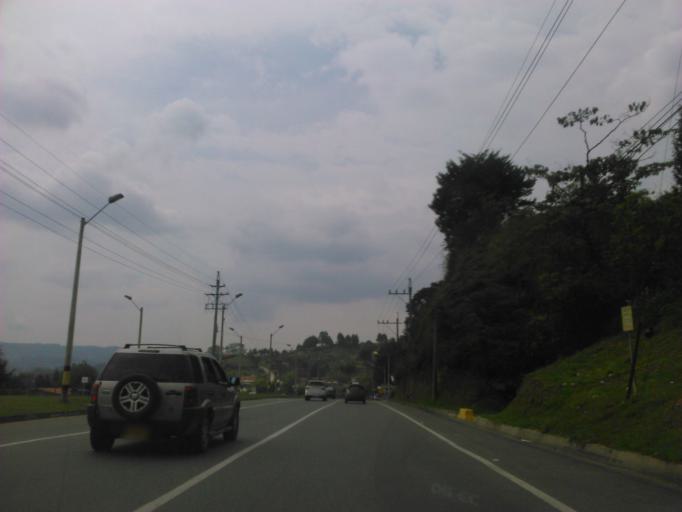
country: CO
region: Antioquia
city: San Vicente
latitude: 6.2258
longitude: -75.3940
